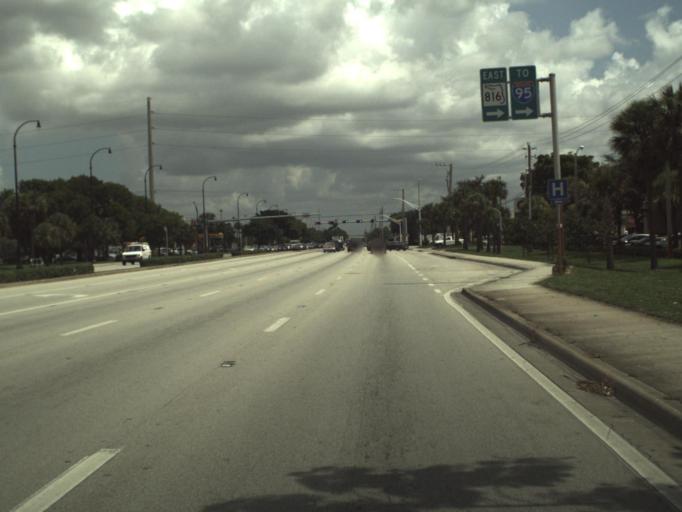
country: US
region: Florida
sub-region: Broward County
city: Lauderdale Lakes
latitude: 26.1629
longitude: -80.2030
